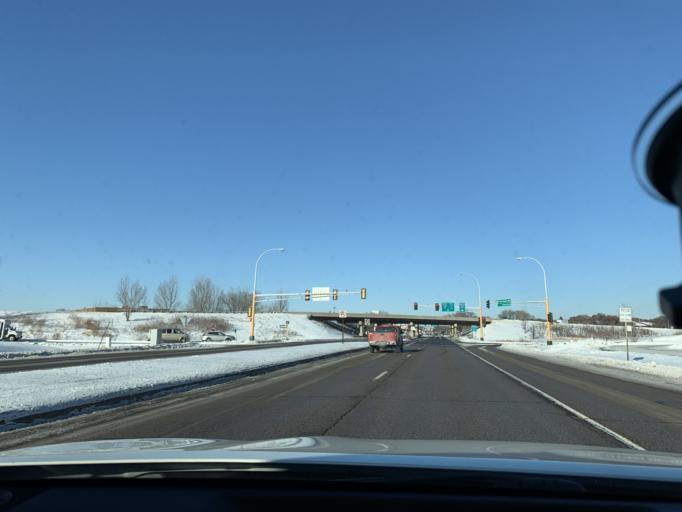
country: US
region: Minnesota
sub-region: Anoka County
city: Coon Rapids
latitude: 45.1346
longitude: -93.2685
